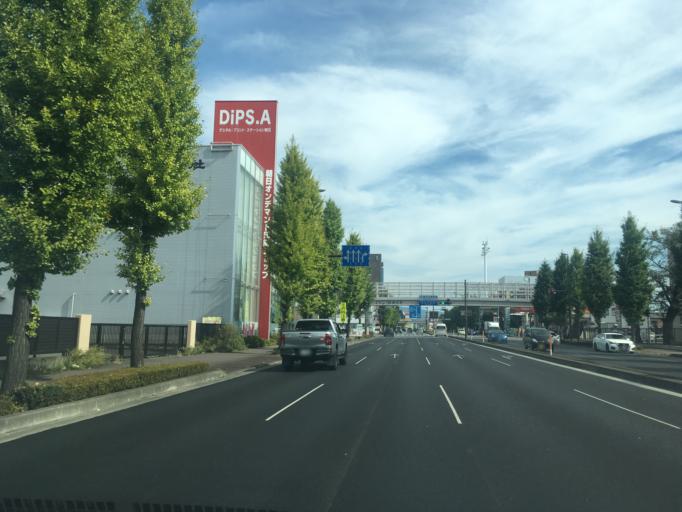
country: JP
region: Gunma
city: Maebashi-shi
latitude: 36.3826
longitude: 139.0420
